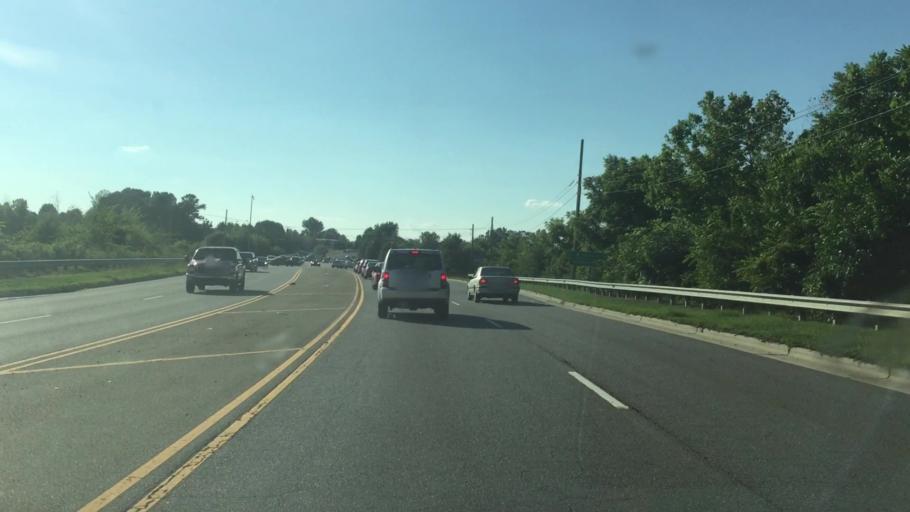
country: US
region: North Carolina
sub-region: Cabarrus County
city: Kannapolis
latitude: 35.4176
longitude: -80.6702
